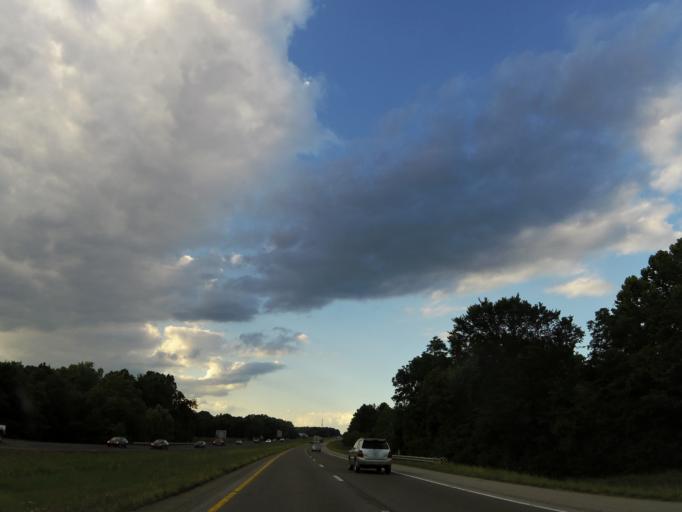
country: US
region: Tennessee
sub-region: Maury County
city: Spring Hill
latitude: 35.6646
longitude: -86.8920
